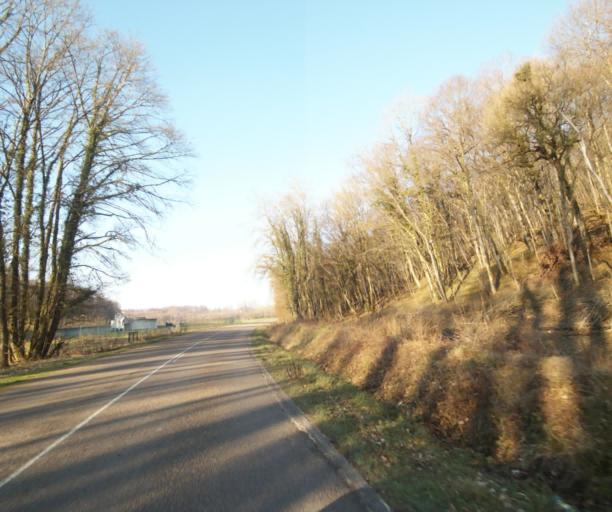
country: FR
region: Champagne-Ardenne
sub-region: Departement de la Haute-Marne
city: Chevillon
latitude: 48.5316
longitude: 5.1068
